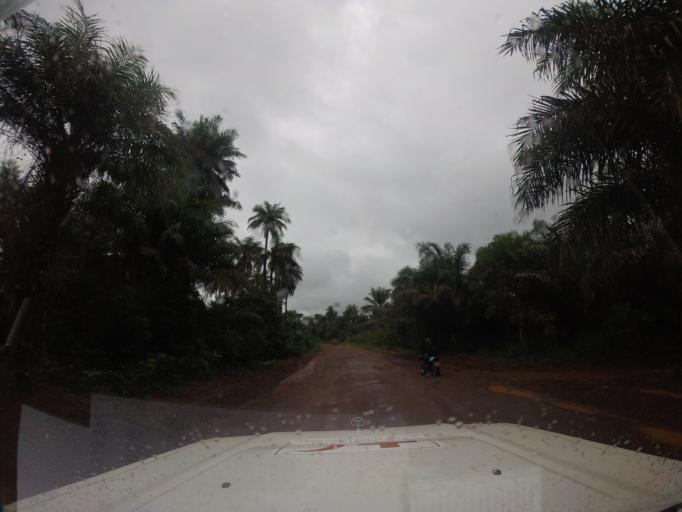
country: SL
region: Northern Province
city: Kambia
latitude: 9.1320
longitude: -12.8842
